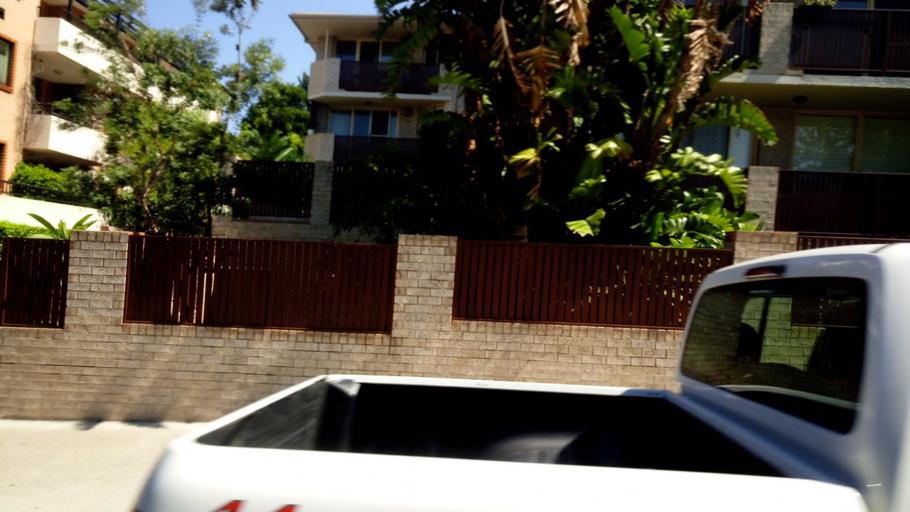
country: AU
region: New South Wales
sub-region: Waverley
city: Bondi Beach
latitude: -33.8948
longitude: 151.2693
